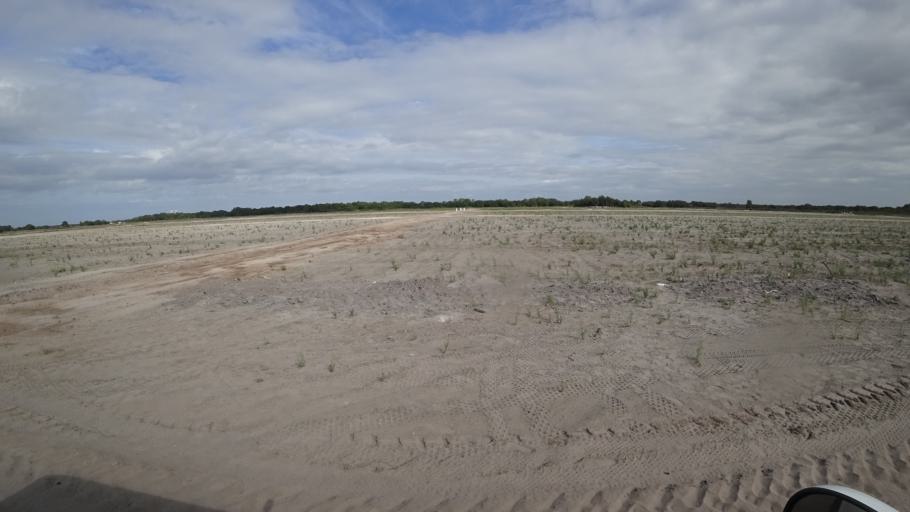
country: US
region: Florida
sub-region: Hillsborough County
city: Wimauma
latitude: 27.5641
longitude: -82.3039
